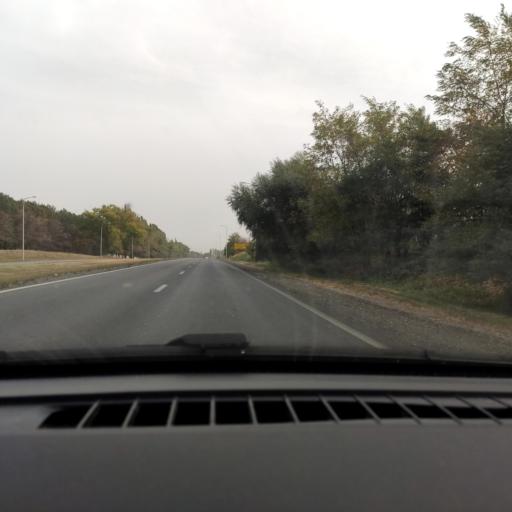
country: RU
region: Belgorod
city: Razumnoye
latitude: 50.6643
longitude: 36.7056
